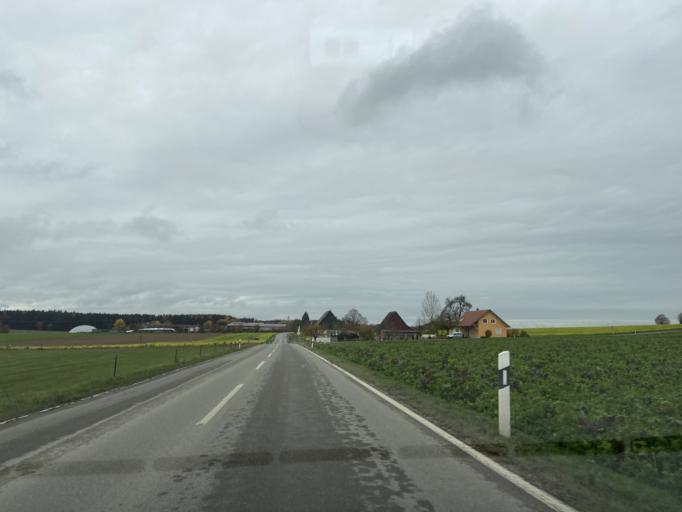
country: DE
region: Baden-Wuerttemberg
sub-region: Tuebingen Region
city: Wald
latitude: 47.9651
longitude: 9.1939
